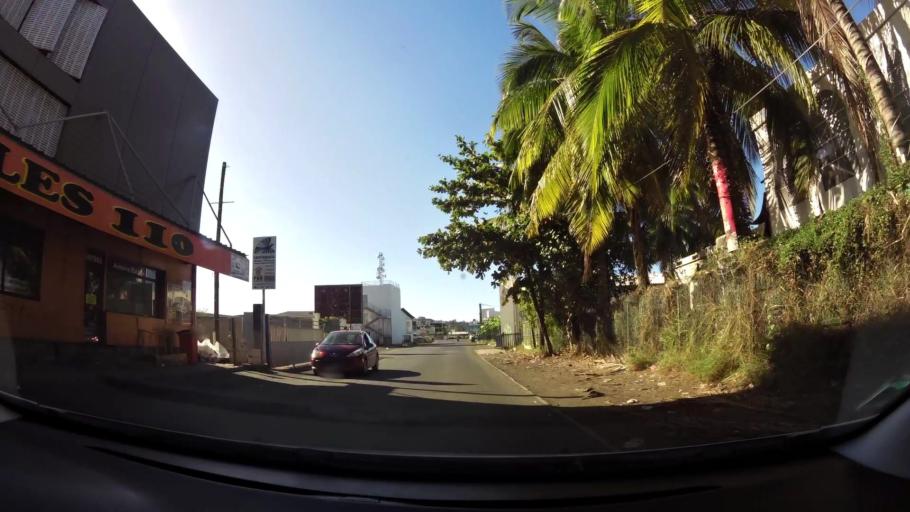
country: YT
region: Mamoudzou
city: Mamoudzou
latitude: -12.7739
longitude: 45.2248
